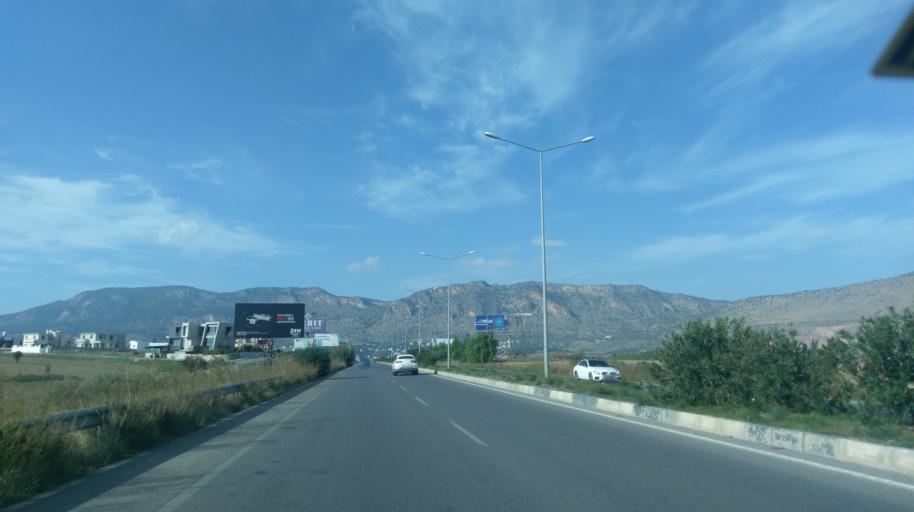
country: CY
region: Keryneia
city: Kyrenia
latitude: 35.2679
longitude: 33.2919
